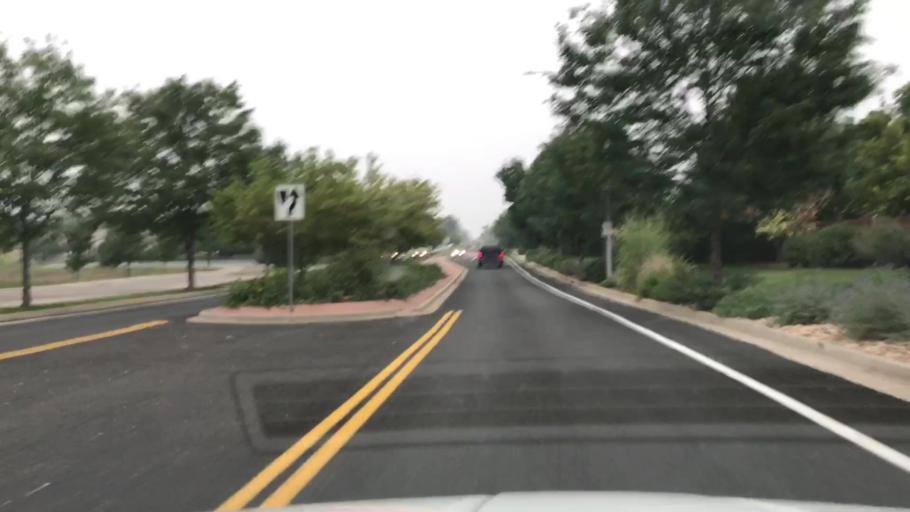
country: US
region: Colorado
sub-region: Broomfield County
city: Broomfield
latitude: 39.9475
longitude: -105.0624
